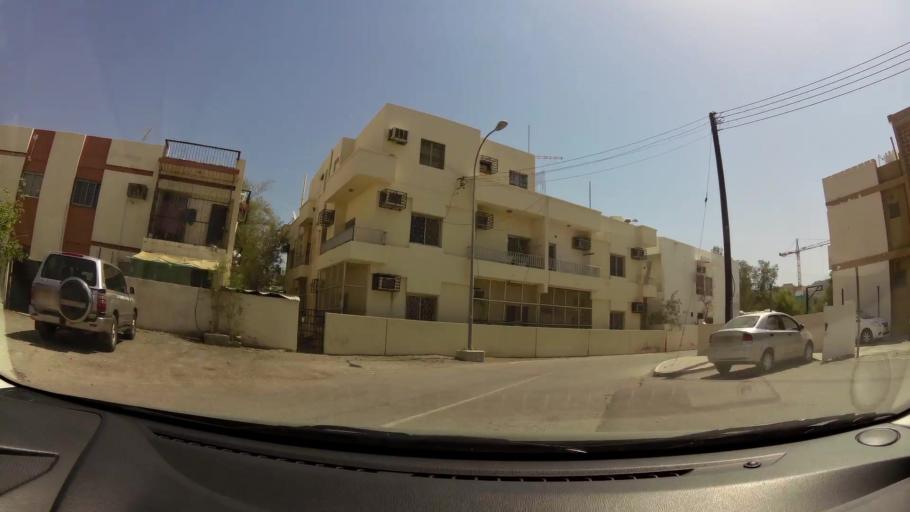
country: OM
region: Muhafazat Masqat
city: Muscat
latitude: 23.5996
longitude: 58.5443
